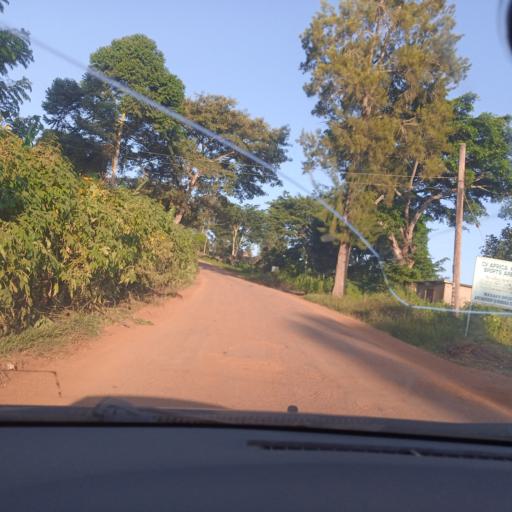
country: UG
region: Central Region
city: Masaka
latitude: -0.3356
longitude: 31.7602
